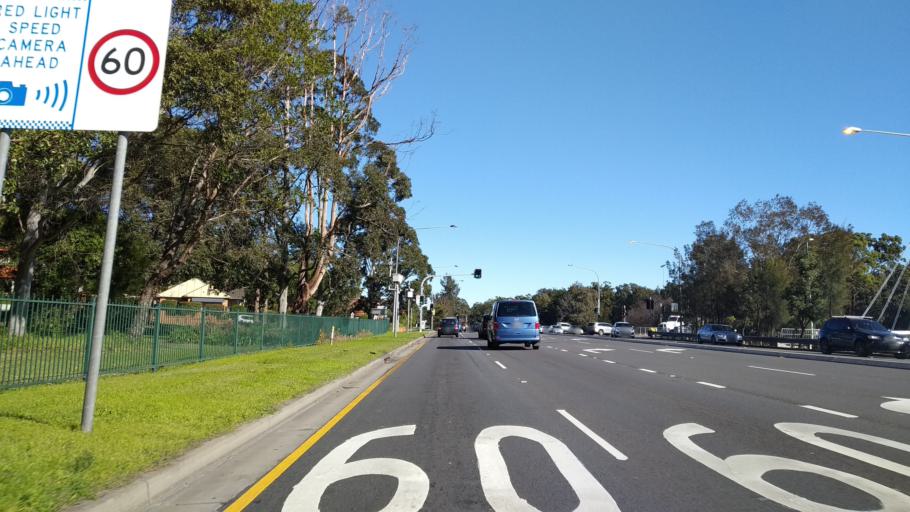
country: AU
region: New South Wales
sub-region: Leichhardt
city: Leichhardt
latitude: -33.8706
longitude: 151.1428
